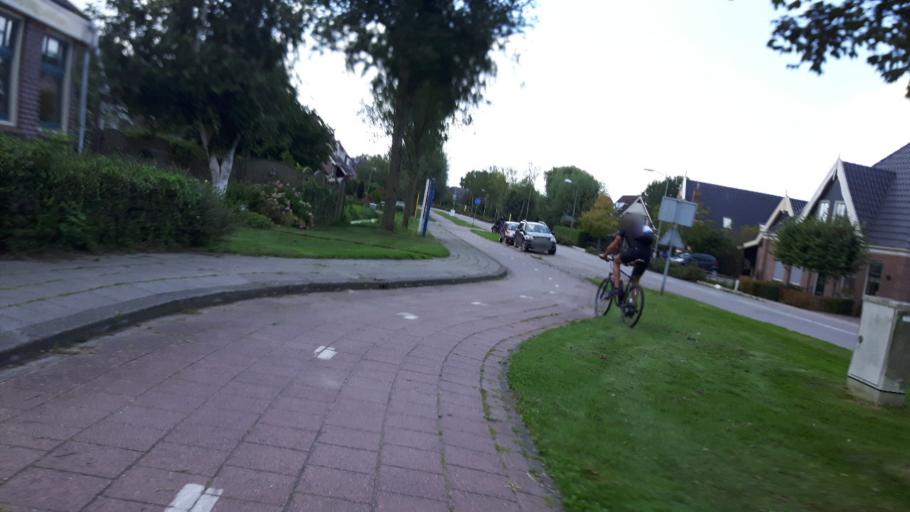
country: NL
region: North Holland
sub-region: Gemeente Medemblik
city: Medemblik
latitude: 52.7415
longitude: 5.1400
